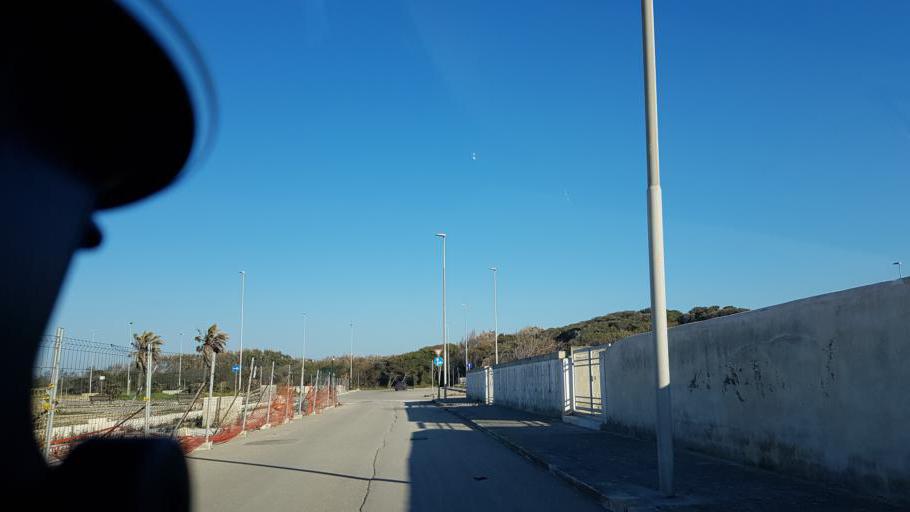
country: IT
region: Apulia
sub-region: Provincia di Lecce
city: Struda
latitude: 40.3949
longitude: 18.2974
